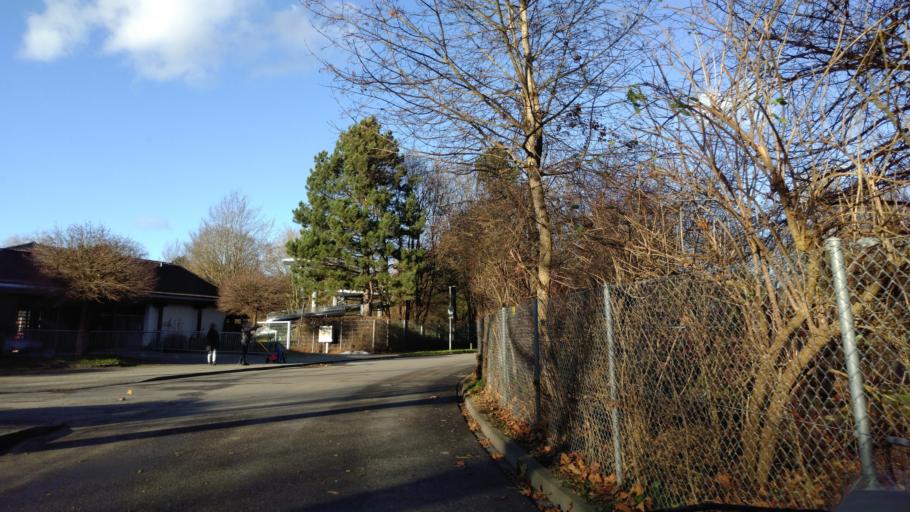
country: DE
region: Baden-Wuerttemberg
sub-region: Tuebingen Region
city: Bad Waldsee
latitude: 47.9209
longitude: 9.7624
